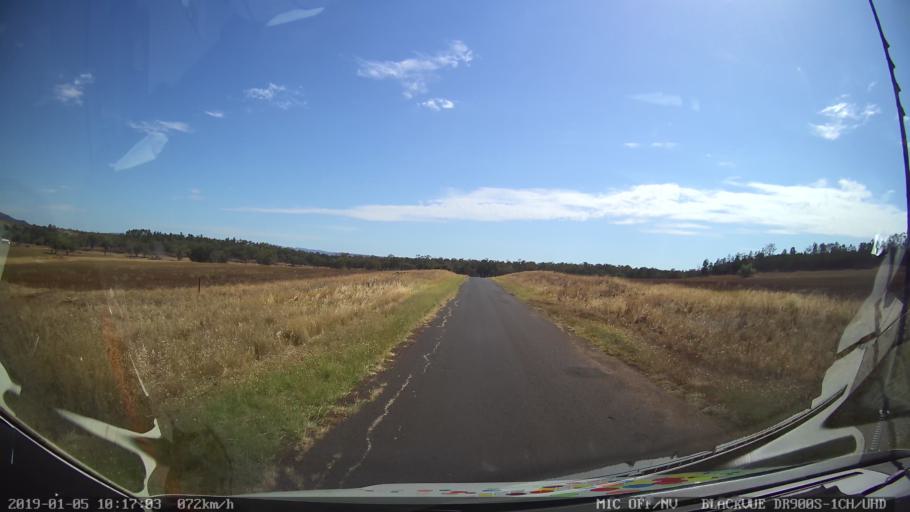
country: AU
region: New South Wales
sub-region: Gilgandra
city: Gilgandra
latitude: -31.5695
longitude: 148.9575
